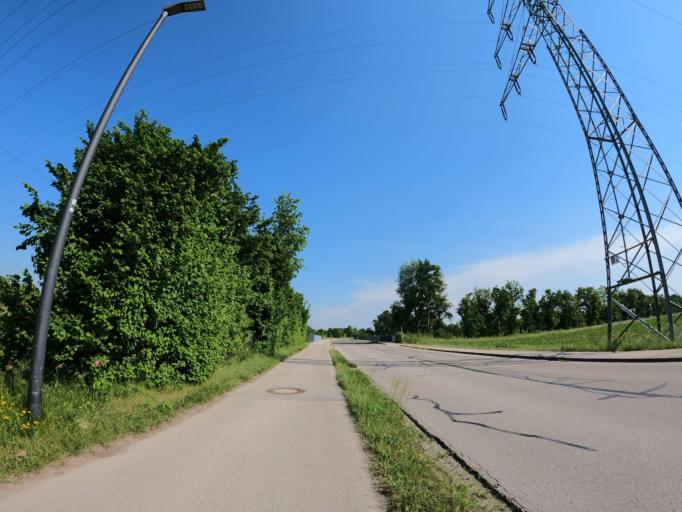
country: DE
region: Bavaria
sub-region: Upper Bavaria
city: Hohenbrunn
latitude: 48.0537
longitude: 11.6911
